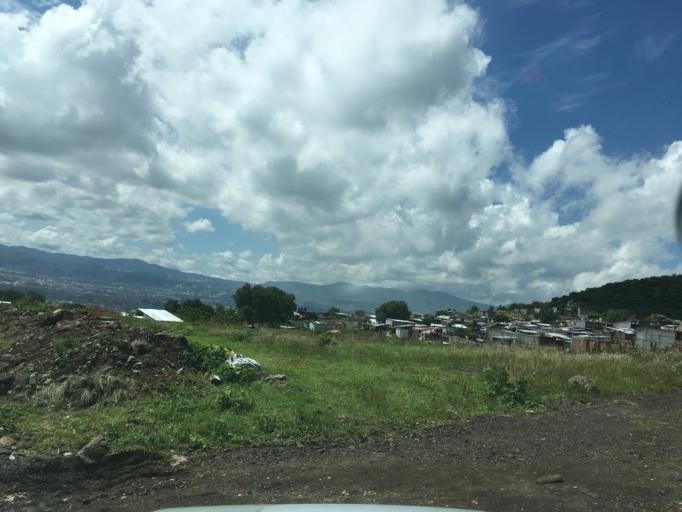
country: MX
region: Michoacan
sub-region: Tarimbaro
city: Fraccionamiento Metropolis II
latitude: 19.7275
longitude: -101.2390
